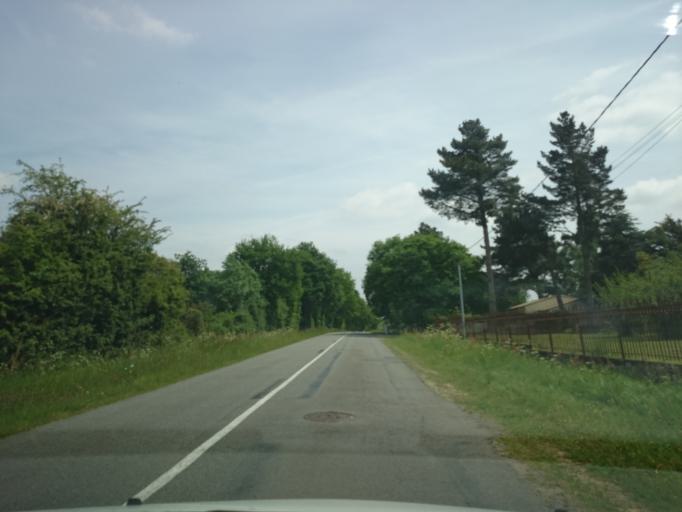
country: FR
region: Pays de la Loire
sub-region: Departement de la Loire-Atlantique
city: Bouaye
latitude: 47.1517
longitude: -1.6560
